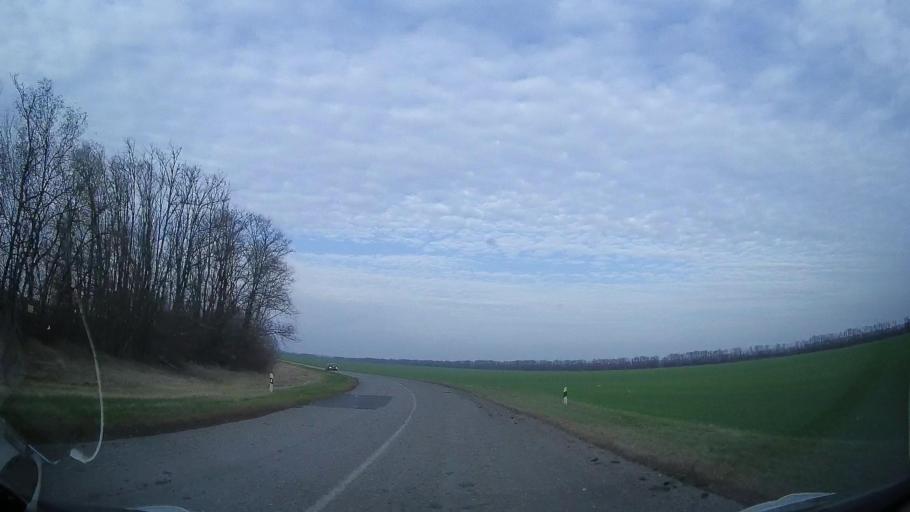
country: RU
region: Rostov
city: Zernograd
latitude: 46.9667
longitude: 40.3912
